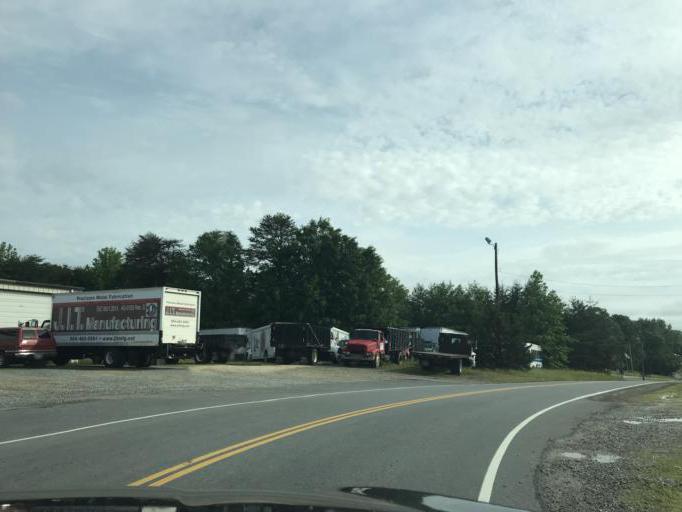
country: US
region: South Carolina
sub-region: Spartanburg County
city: Roebuck
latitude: 34.9107
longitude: -81.9553
